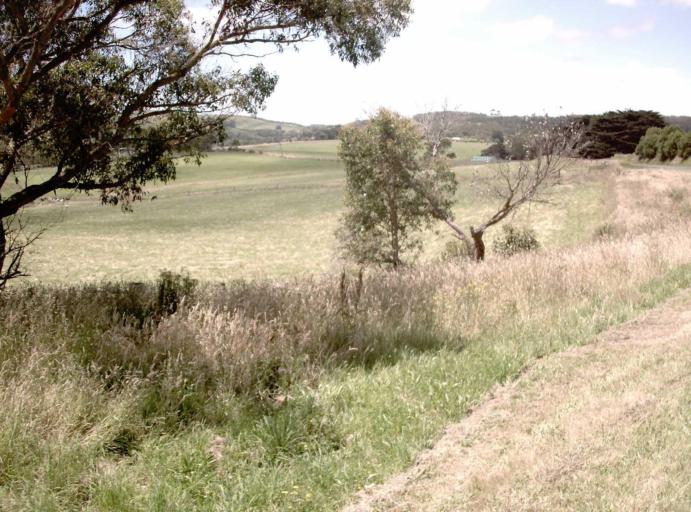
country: AU
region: Victoria
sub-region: Bass Coast
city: North Wonthaggi
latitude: -38.7114
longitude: 146.0902
